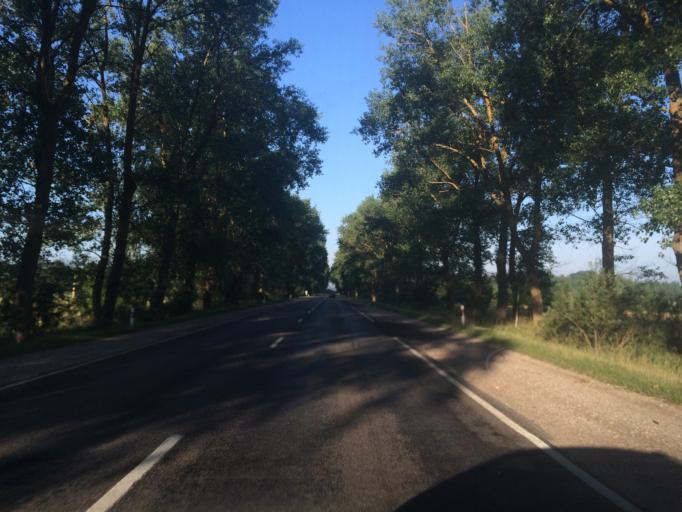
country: LT
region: Utenos apskritis
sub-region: Anyksciai
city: Anyksciai
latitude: 55.3721
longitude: 25.0162
